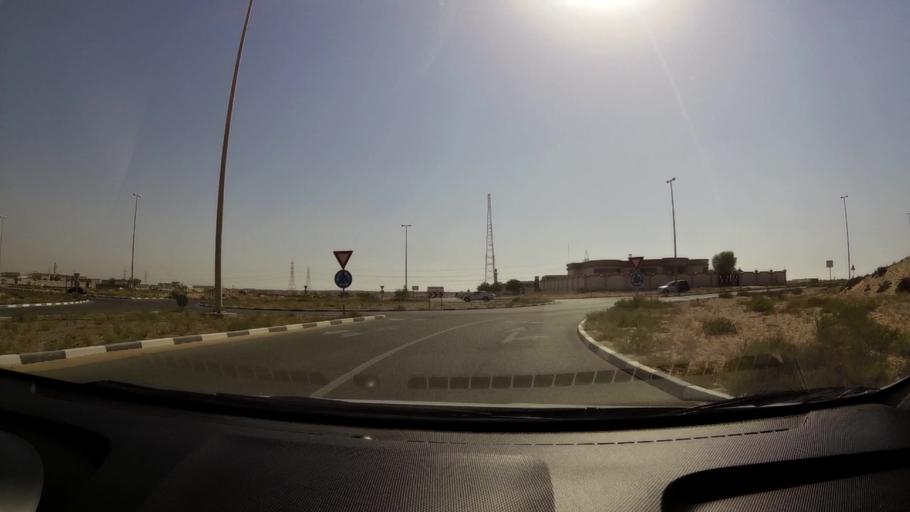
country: AE
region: Umm al Qaywayn
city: Umm al Qaywayn
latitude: 25.4878
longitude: 55.5841
